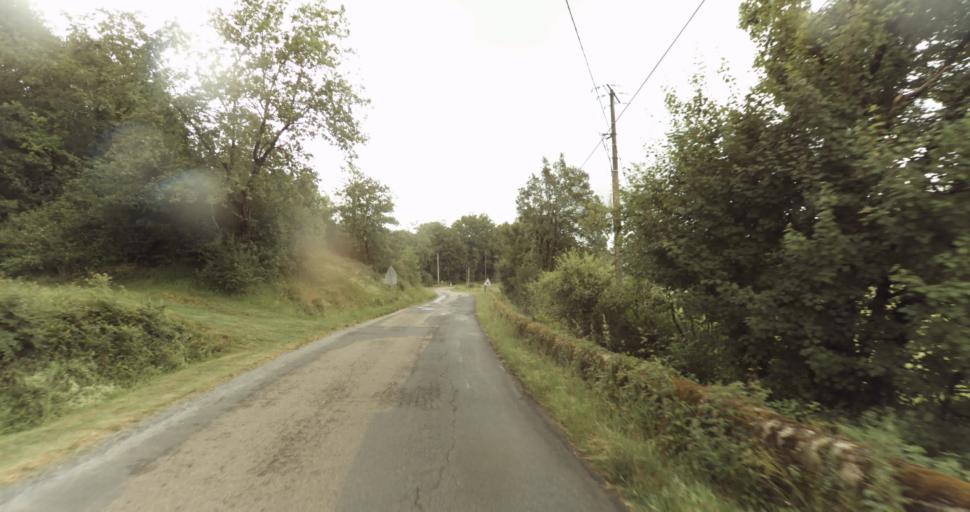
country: FR
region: Aquitaine
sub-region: Departement de la Dordogne
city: Belves
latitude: 44.7552
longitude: 0.9259
